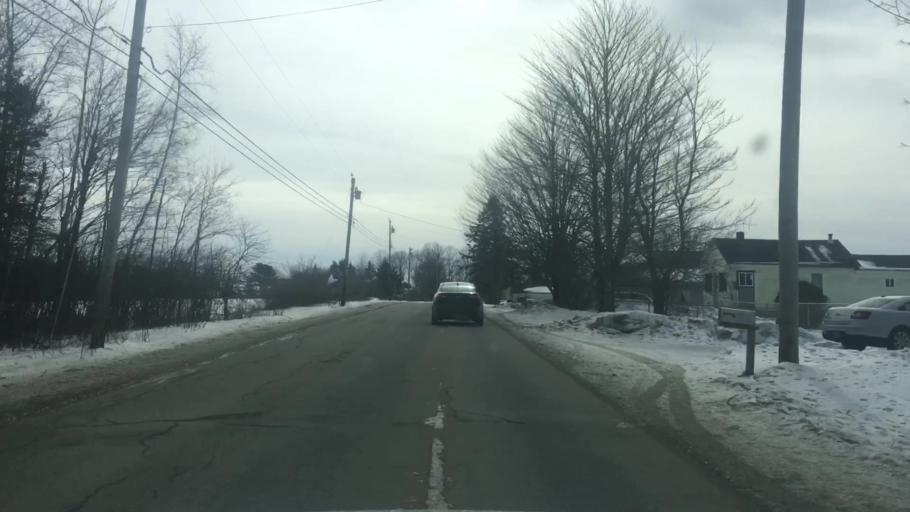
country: US
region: Maine
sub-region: Hancock County
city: Orland
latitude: 44.5797
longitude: -68.7253
